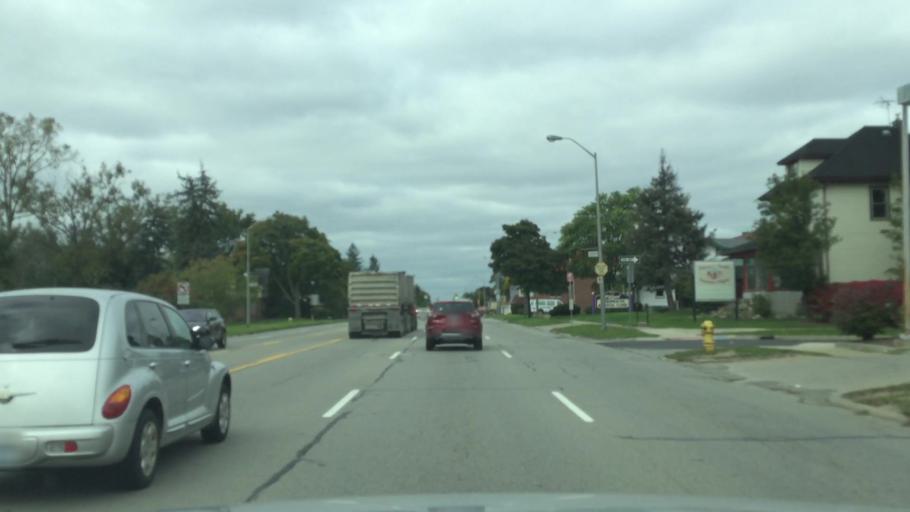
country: US
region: Michigan
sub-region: Oakland County
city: Pontiac
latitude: 42.6357
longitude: -83.3112
